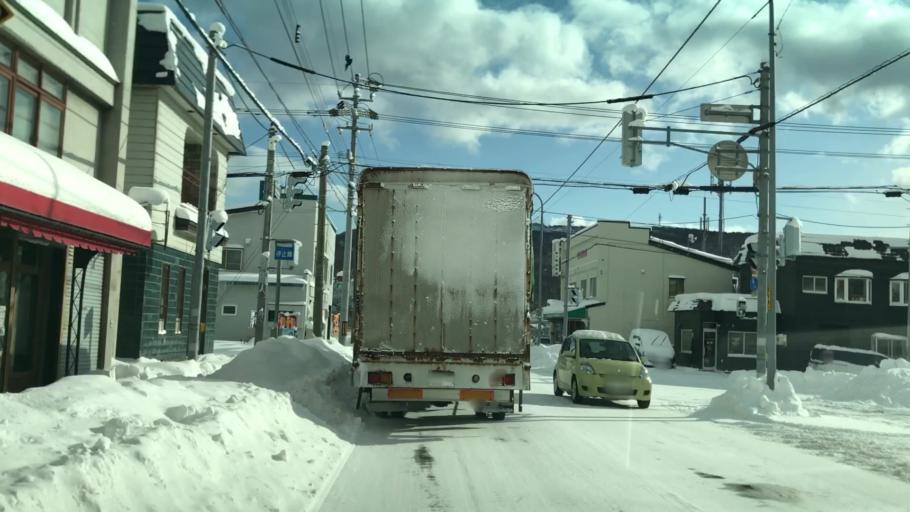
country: JP
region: Hokkaido
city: Yoichi
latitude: 43.2635
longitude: 140.6428
